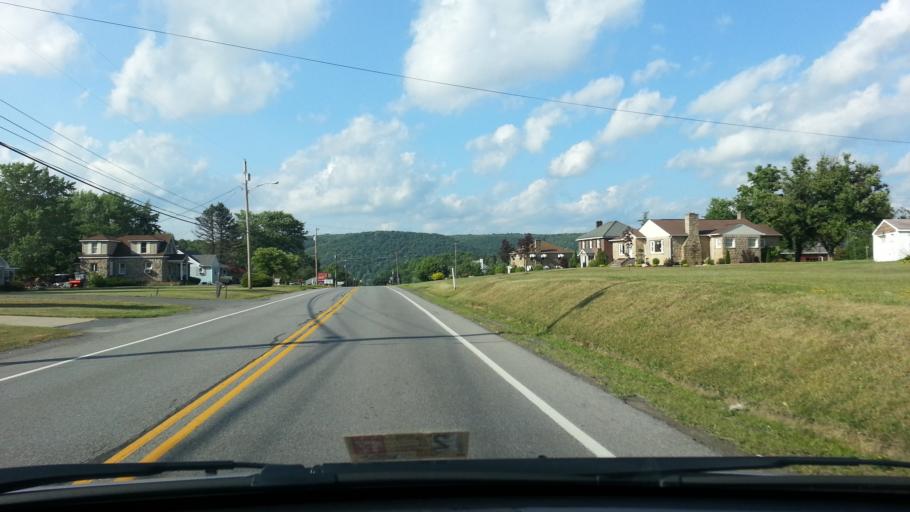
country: US
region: Pennsylvania
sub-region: Elk County
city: Saint Marys
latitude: 41.2650
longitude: -78.4986
